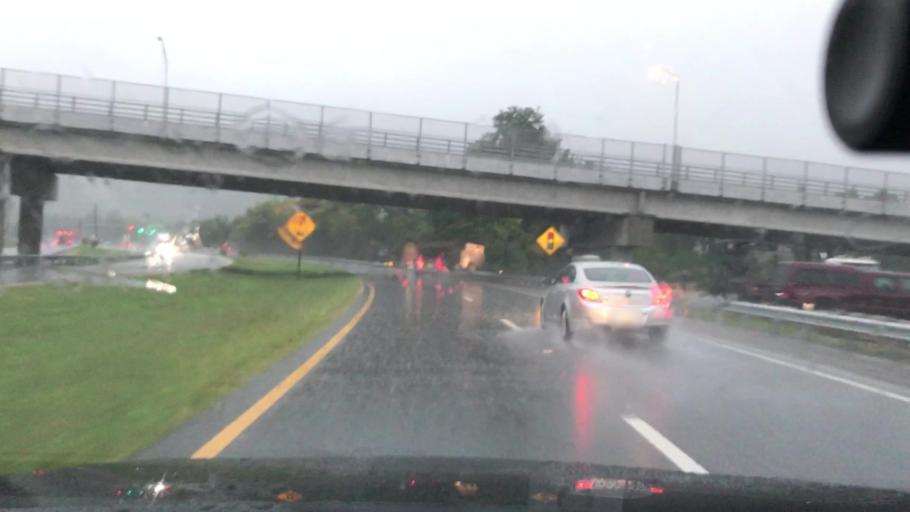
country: US
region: Virginia
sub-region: Giles County
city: Narrows
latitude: 37.3360
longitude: -80.8081
